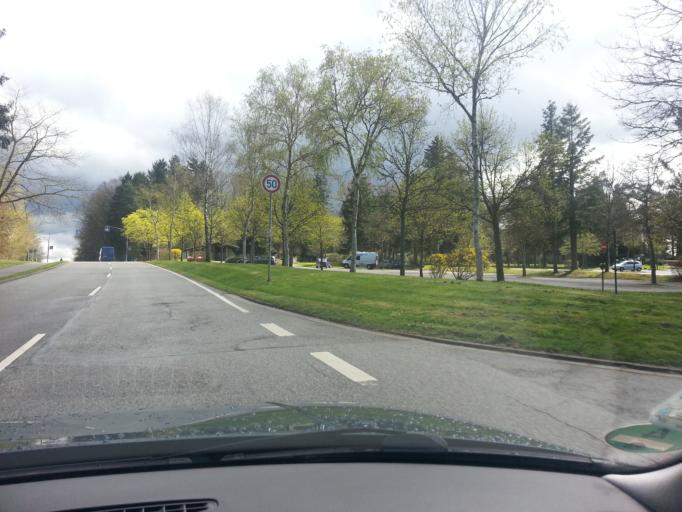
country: DE
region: Saarland
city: Kirkel
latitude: 49.3210
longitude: 7.2189
